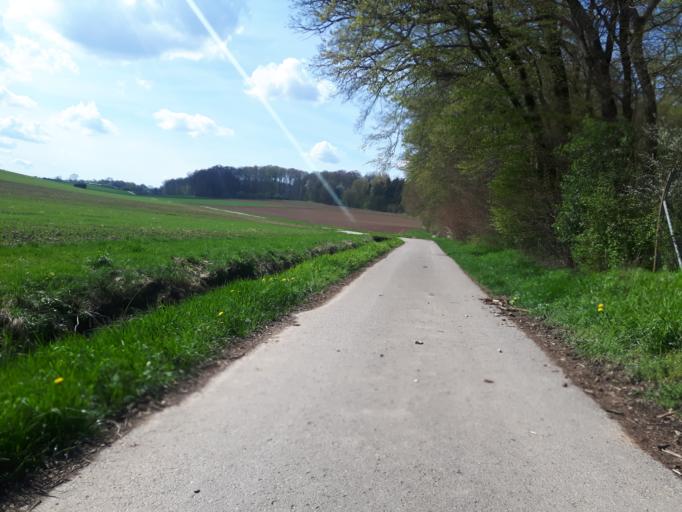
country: DE
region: Baden-Wuerttemberg
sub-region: Regierungsbezirk Stuttgart
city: Schwaigern
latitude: 49.1411
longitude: 9.0197
